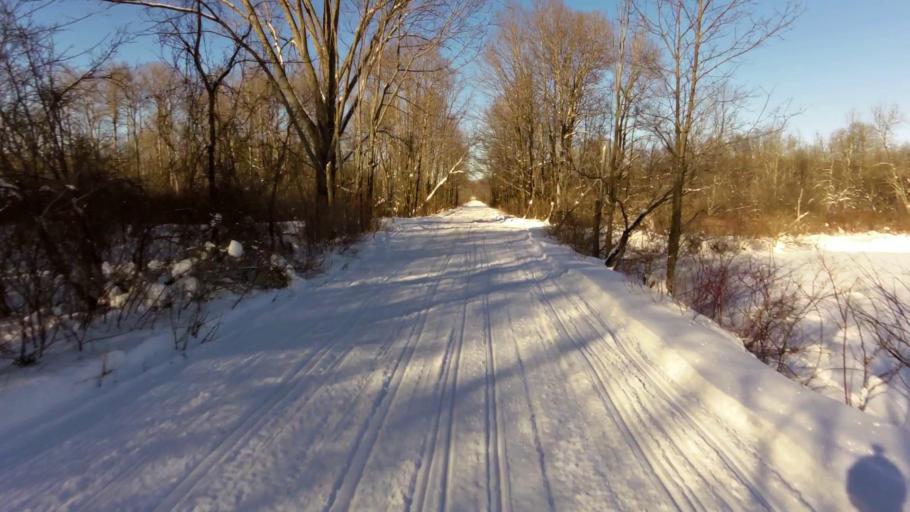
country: US
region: New York
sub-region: Chautauqua County
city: Mayville
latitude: 42.1852
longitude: -79.5793
